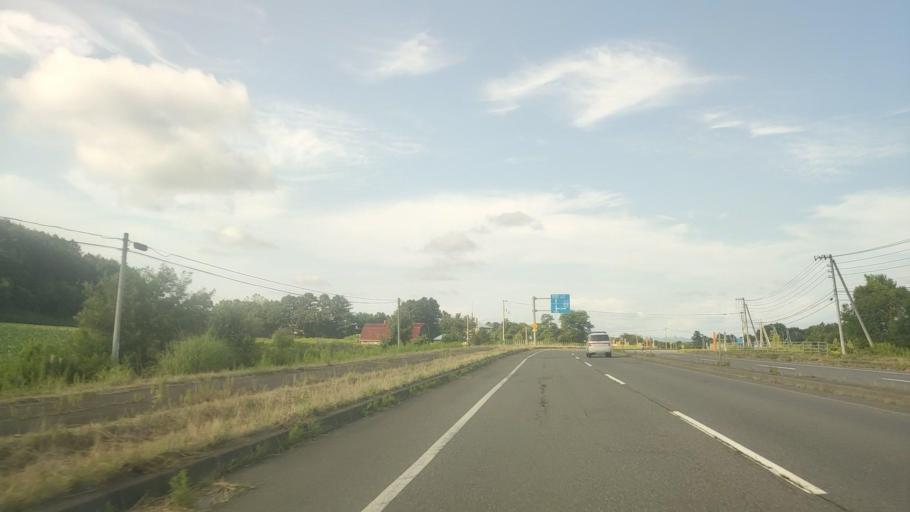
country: JP
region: Hokkaido
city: Chitose
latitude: 42.7744
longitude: 141.8271
